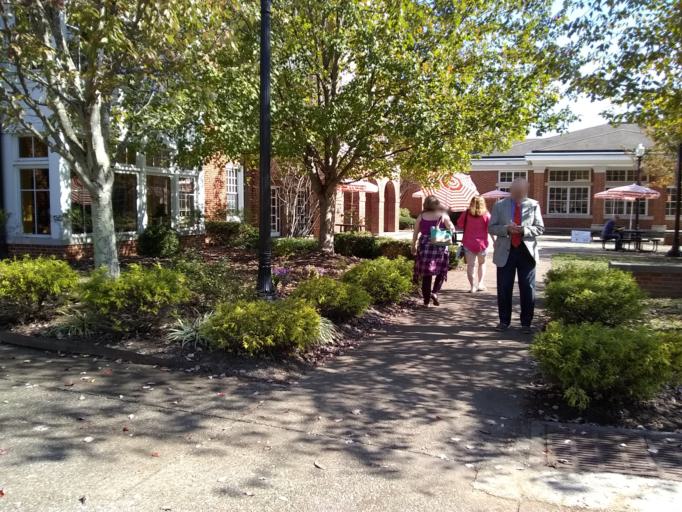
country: US
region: West Virginia
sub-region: Upshur County
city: Buckhannon
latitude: 38.9898
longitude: -80.2171
